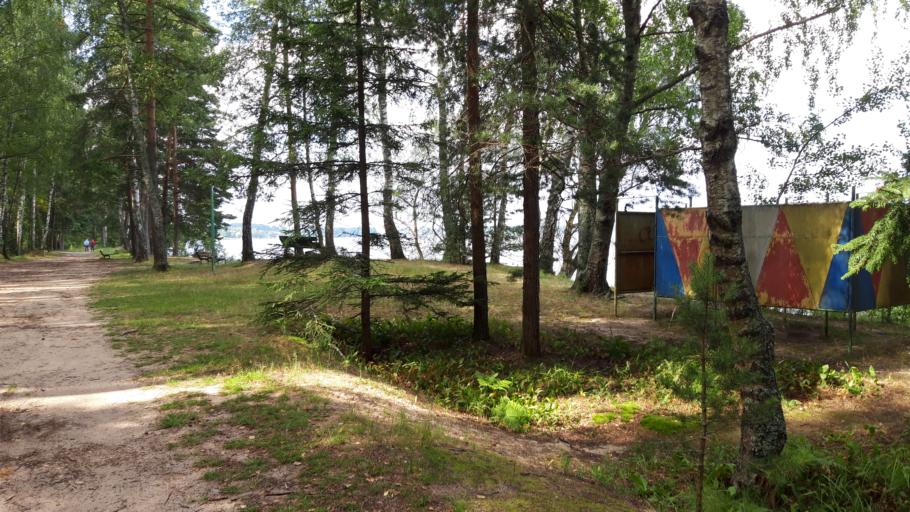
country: RU
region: Tverskaya
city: Konakovo
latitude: 56.6738
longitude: 36.6857
